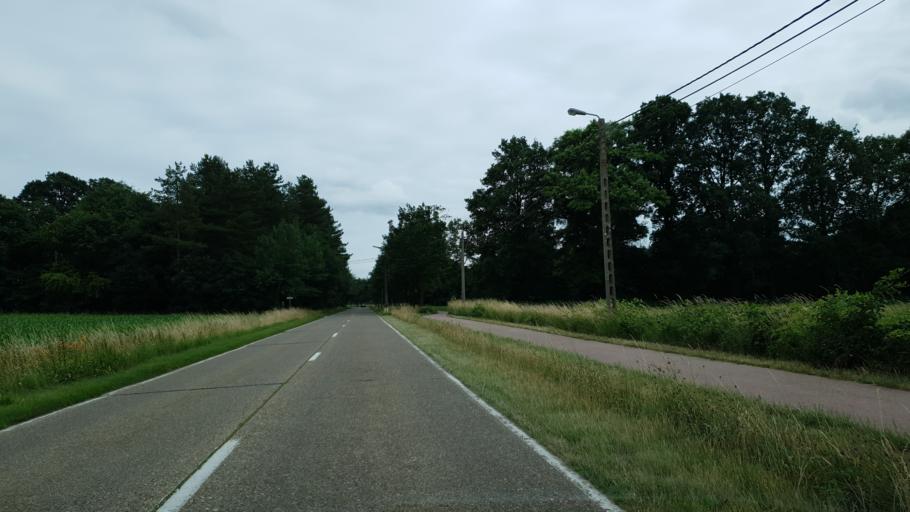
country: BE
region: Flanders
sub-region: Provincie Vlaams-Brabant
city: Scherpenheuvel-Zichem
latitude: 51.0488
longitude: 4.9491
